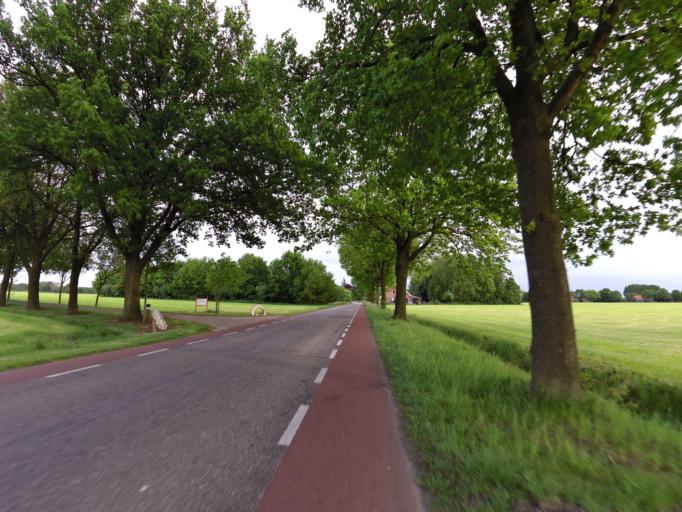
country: NL
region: Gelderland
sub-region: Oude IJsselstreek
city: Gendringen
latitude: 51.8495
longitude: 6.3876
